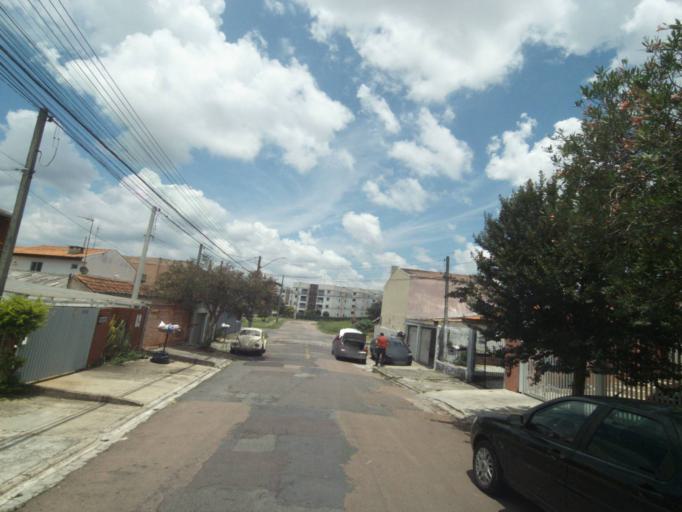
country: BR
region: Parana
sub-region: Curitiba
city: Curitiba
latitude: -25.4700
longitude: -49.3408
